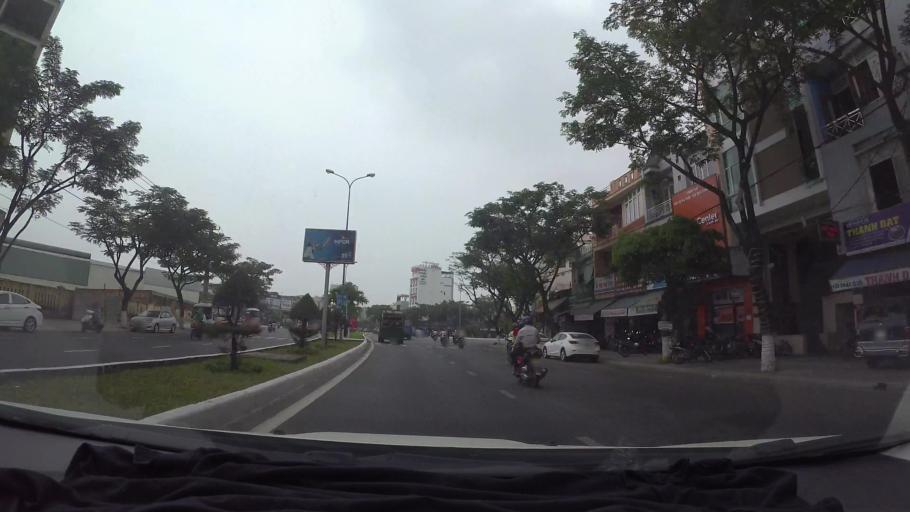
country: VN
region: Da Nang
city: Da Nang
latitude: 16.0557
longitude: 108.2082
